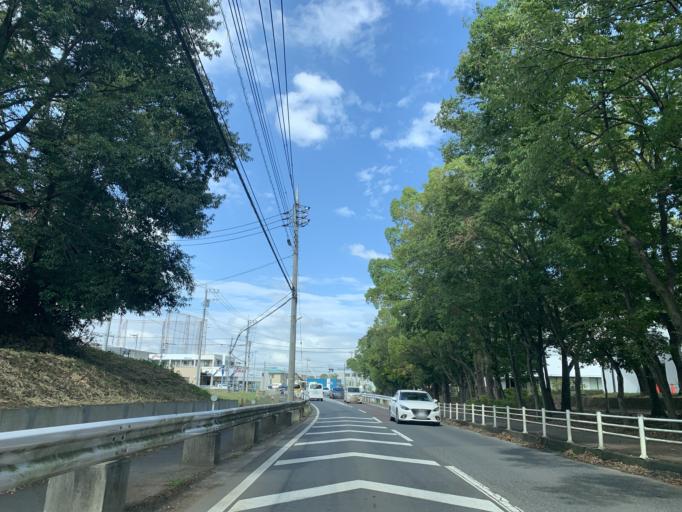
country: JP
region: Chiba
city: Nagareyama
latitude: 35.8581
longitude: 139.9170
